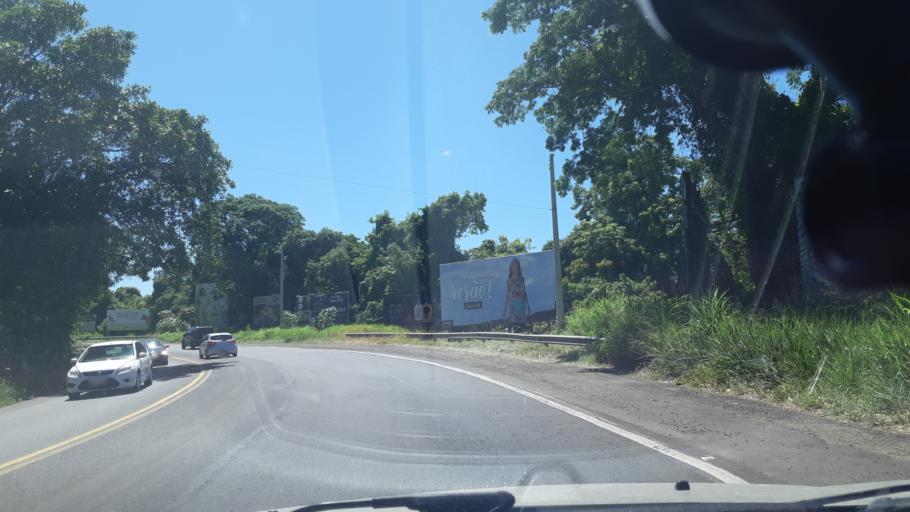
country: BR
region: Rio Grande do Sul
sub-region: Estancia Velha
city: Estancia Velha
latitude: -29.6284
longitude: -51.1400
